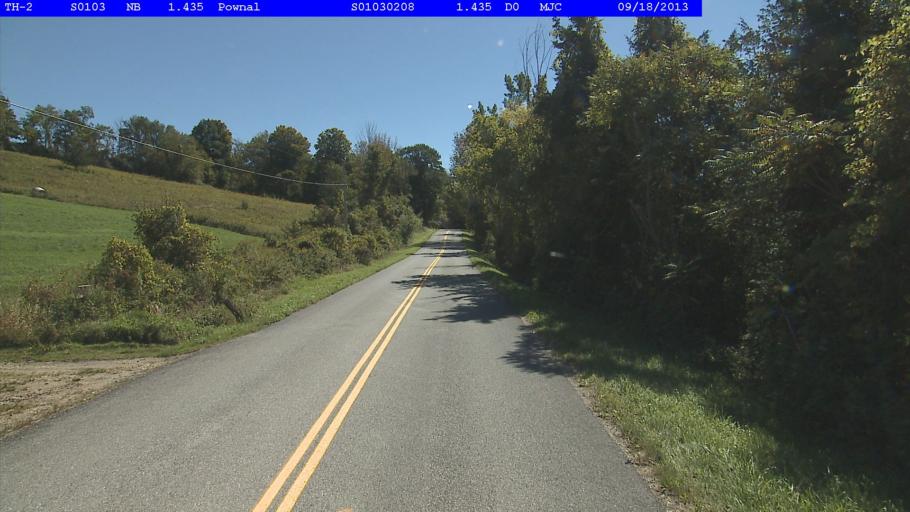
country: US
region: Vermont
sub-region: Bennington County
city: Bennington
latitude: 42.8028
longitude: -73.2448
